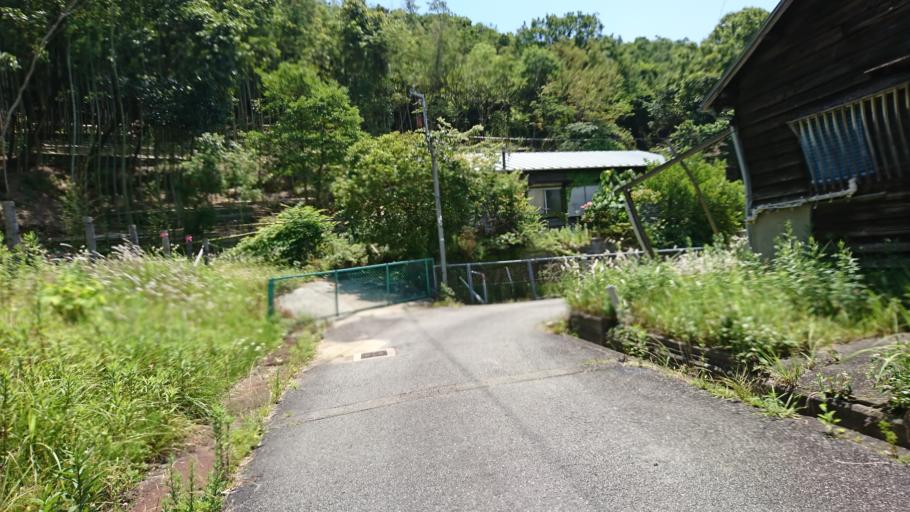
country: JP
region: Hyogo
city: Kakogawacho-honmachi
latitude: 34.8002
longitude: 134.7930
